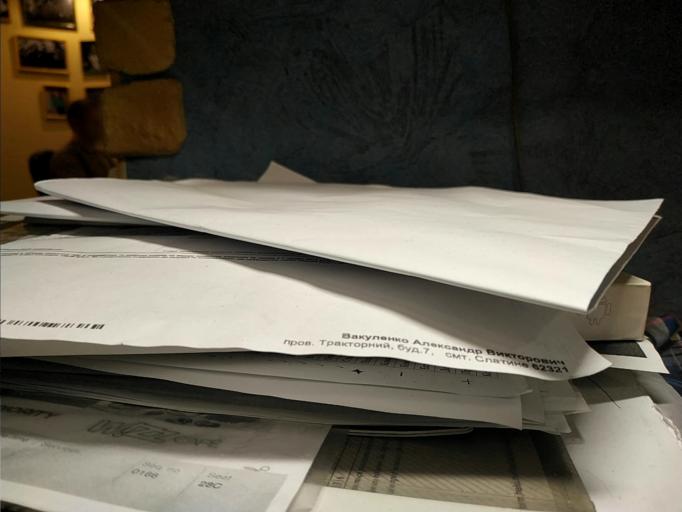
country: RU
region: Tverskaya
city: Zubtsov
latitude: 56.1119
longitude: 34.6210
